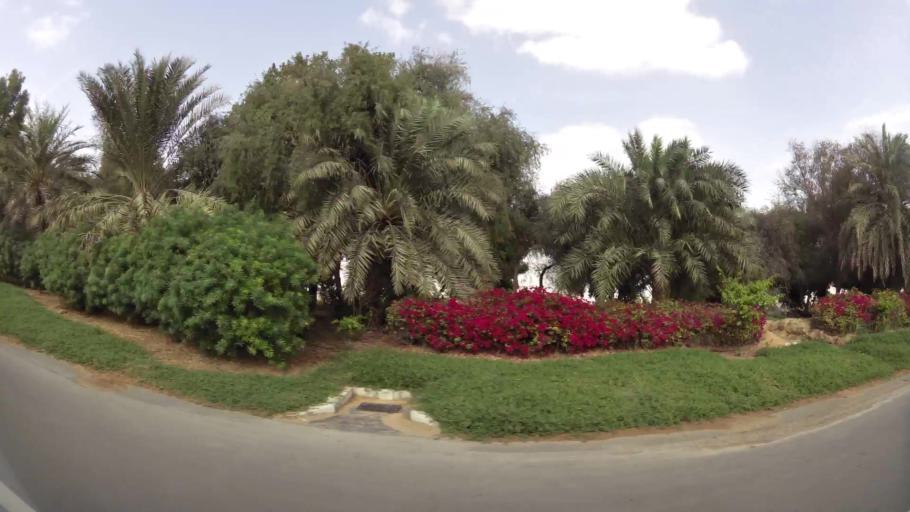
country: AE
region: Abu Dhabi
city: Abu Dhabi
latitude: 24.3964
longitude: 54.5337
